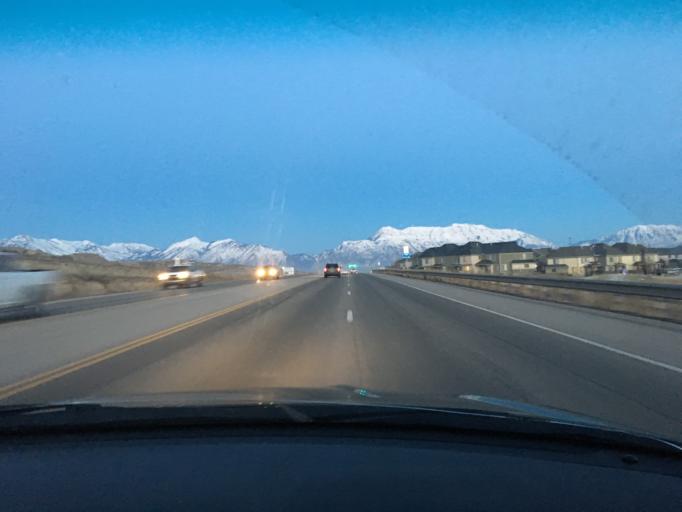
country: US
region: Utah
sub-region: Utah County
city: Saratoga Springs
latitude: 40.3815
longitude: -111.9688
